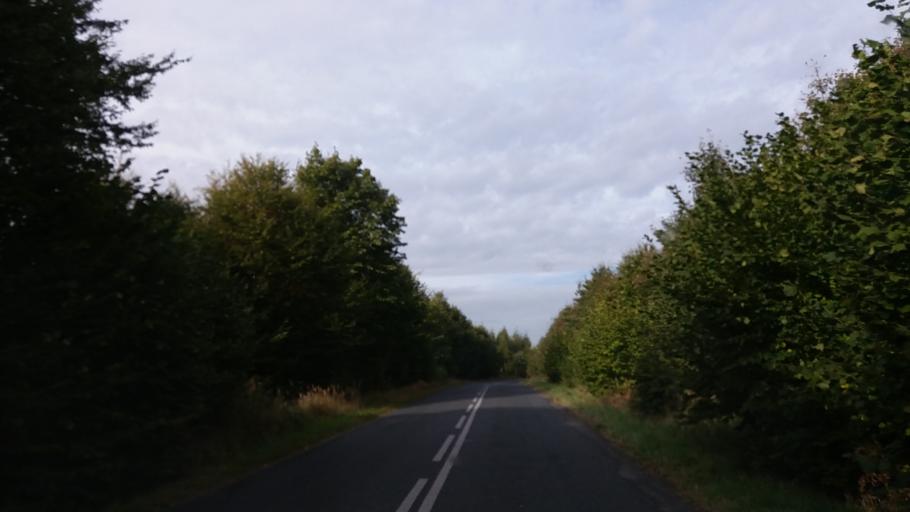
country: PL
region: West Pomeranian Voivodeship
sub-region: Powiat choszczenski
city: Krzecin
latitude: 53.0029
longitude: 15.5005
